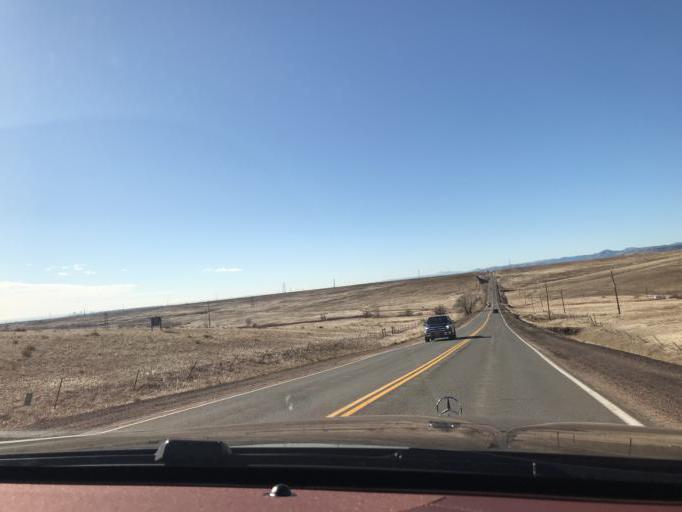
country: US
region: Colorado
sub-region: Boulder County
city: Superior
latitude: 39.9059
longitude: -105.1657
